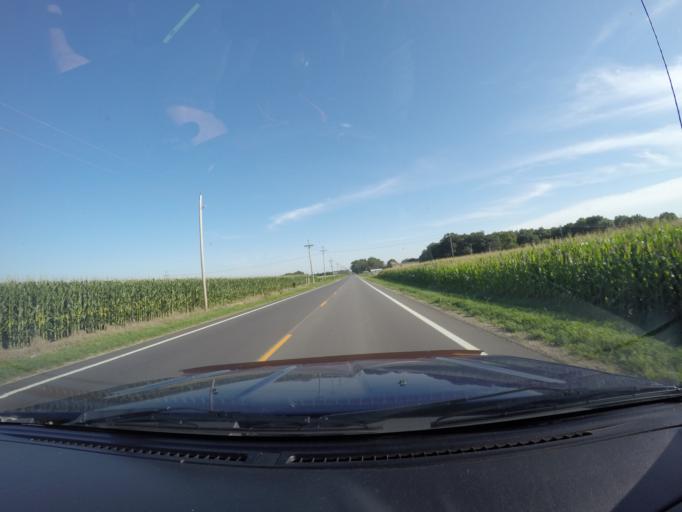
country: US
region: Kansas
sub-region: Douglas County
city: Lawrence
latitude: 39.0163
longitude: -95.2336
